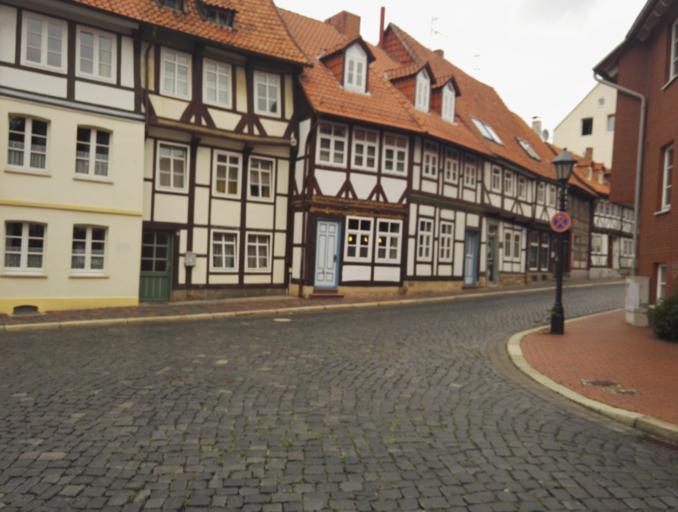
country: DE
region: Lower Saxony
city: Hildesheim
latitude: 52.1463
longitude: 9.9513
